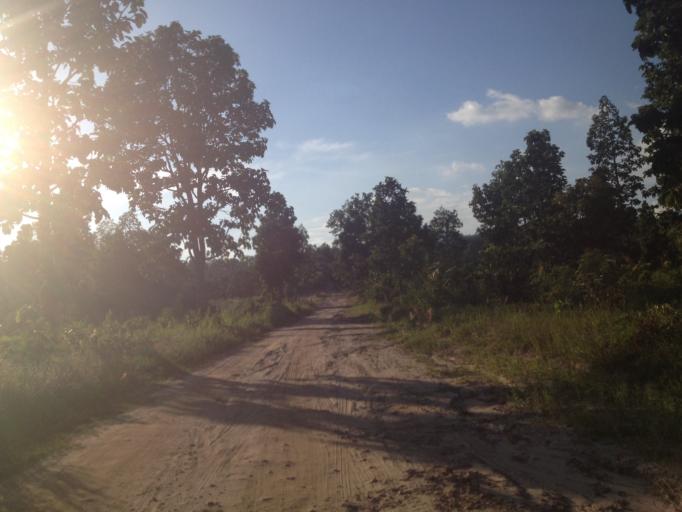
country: TH
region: Chiang Mai
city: Hang Dong
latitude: 18.6921
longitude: 98.8836
